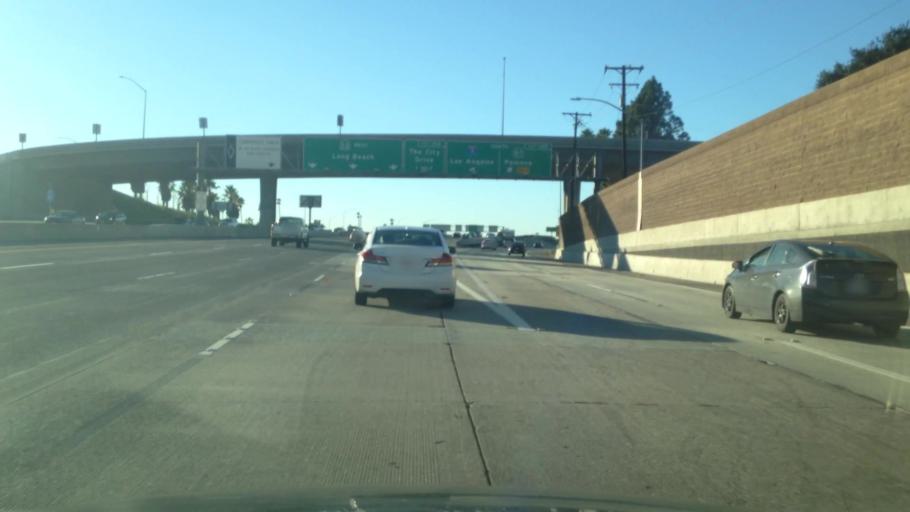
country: US
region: California
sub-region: Orange County
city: Orange
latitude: 33.7784
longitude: -117.8704
